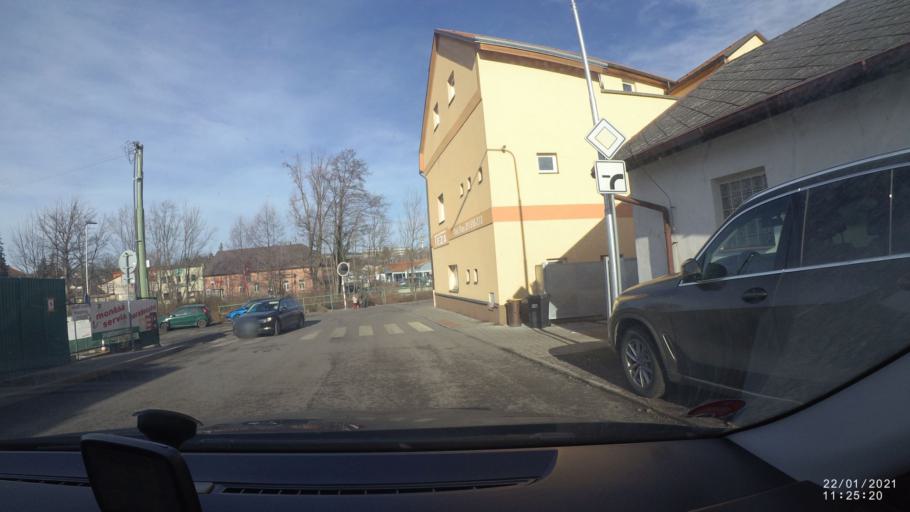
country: CZ
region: Central Bohemia
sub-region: Okres Beroun
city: Horovice
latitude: 49.8371
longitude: 13.8981
